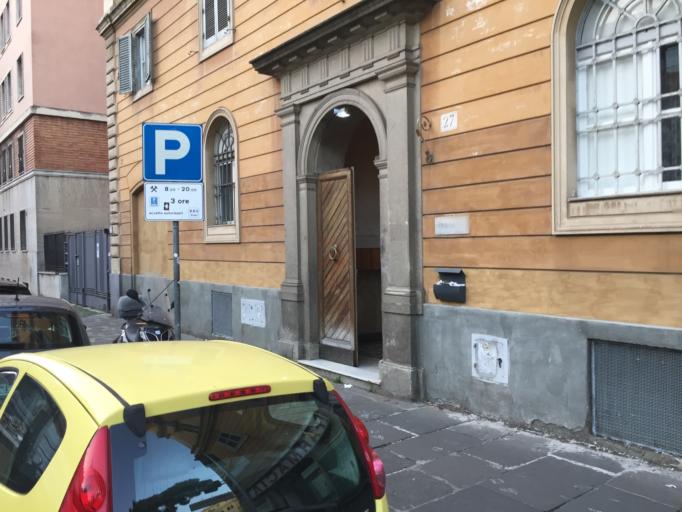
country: VA
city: Vatican City
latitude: 41.9090
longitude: 12.4646
